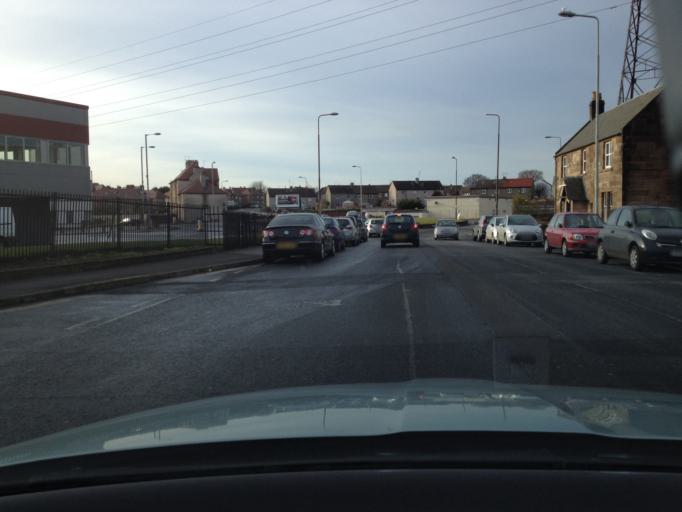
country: GB
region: Scotland
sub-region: Edinburgh
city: Colinton
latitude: 55.9253
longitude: -3.2640
